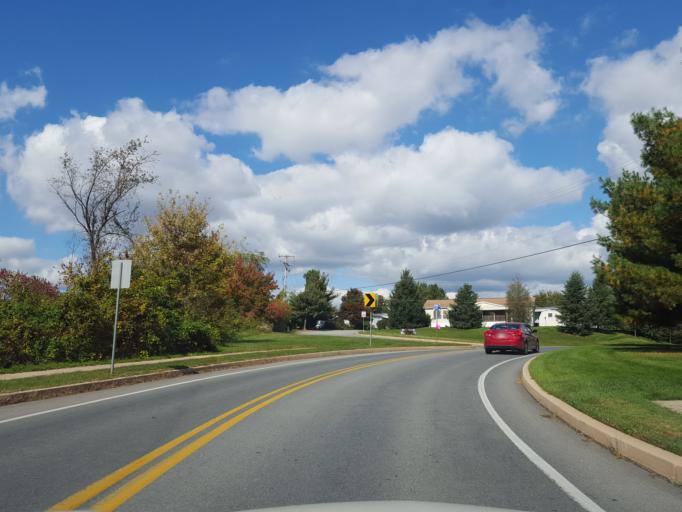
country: US
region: Pennsylvania
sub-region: York County
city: Spry
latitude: 39.9394
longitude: -76.6664
